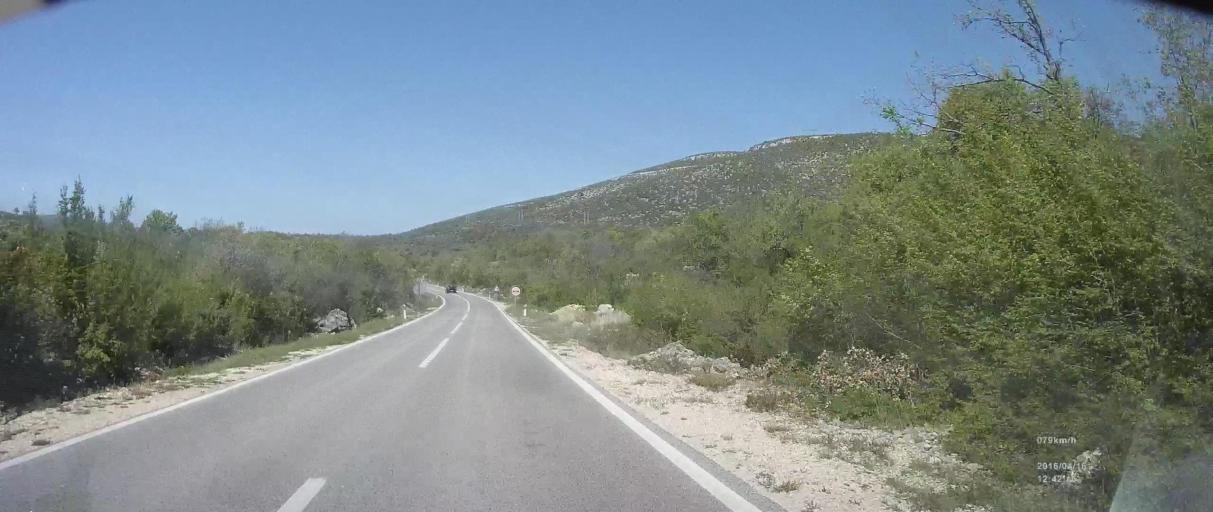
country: HR
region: Sibensko-Kniniska
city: Rogoznica
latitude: 43.6279
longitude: 16.0916
